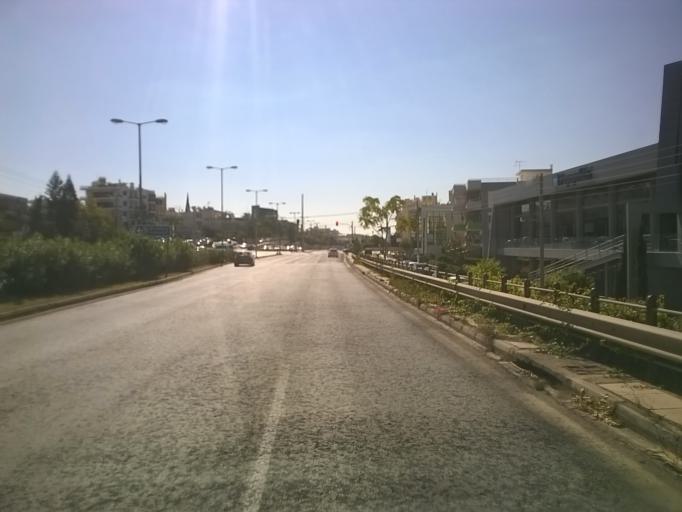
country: GR
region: Attica
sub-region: Nomarchia Anatolikis Attikis
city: Voula
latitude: 37.8426
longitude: 23.7713
